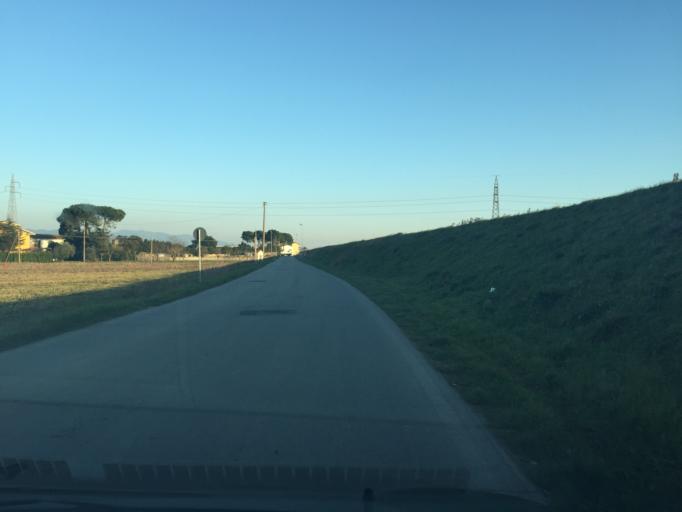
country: IT
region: Tuscany
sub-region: Provincia di Pistoia
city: Ponte Buggianese
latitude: 43.8379
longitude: 10.7533
